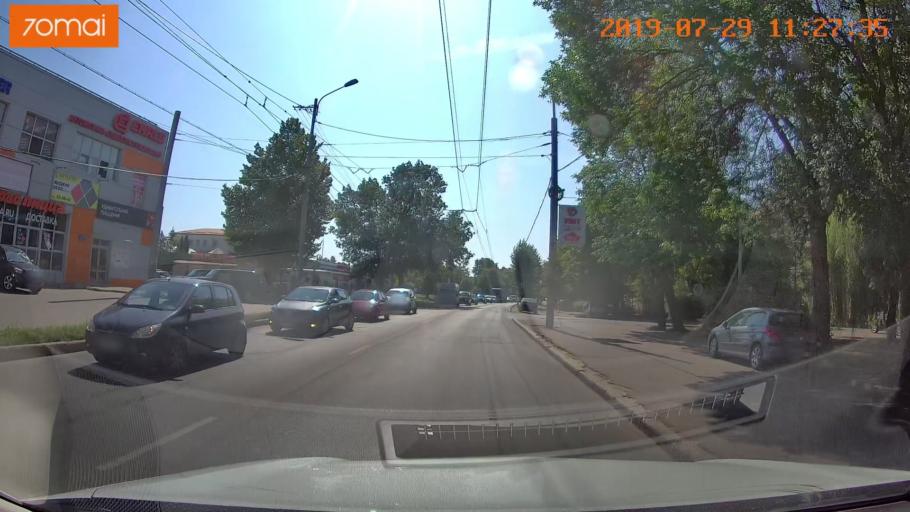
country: RU
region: Kaliningrad
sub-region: Gorod Kaliningrad
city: Kaliningrad
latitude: 54.6906
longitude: 20.5303
